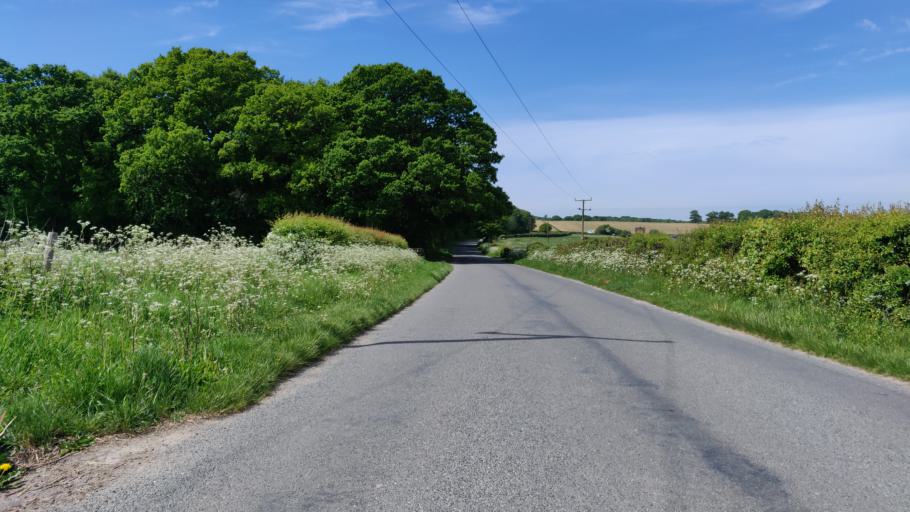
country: GB
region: England
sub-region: West Sussex
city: Southwater
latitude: 51.0471
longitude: -0.3706
